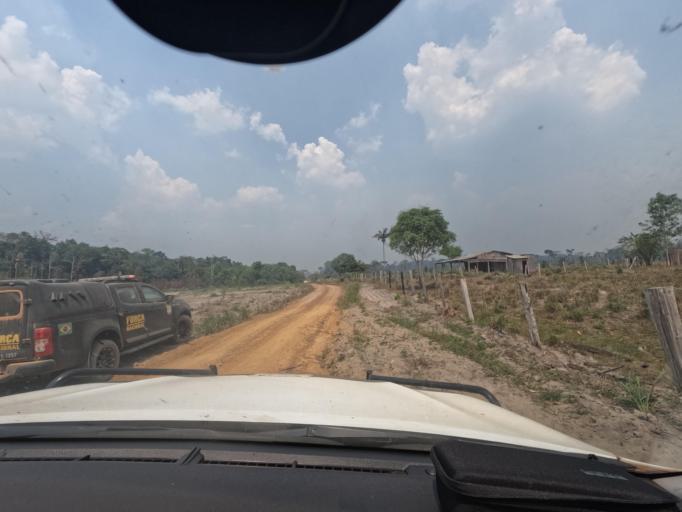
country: BR
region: Rondonia
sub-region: Porto Velho
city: Porto Velho
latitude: -8.7738
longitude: -63.1036
